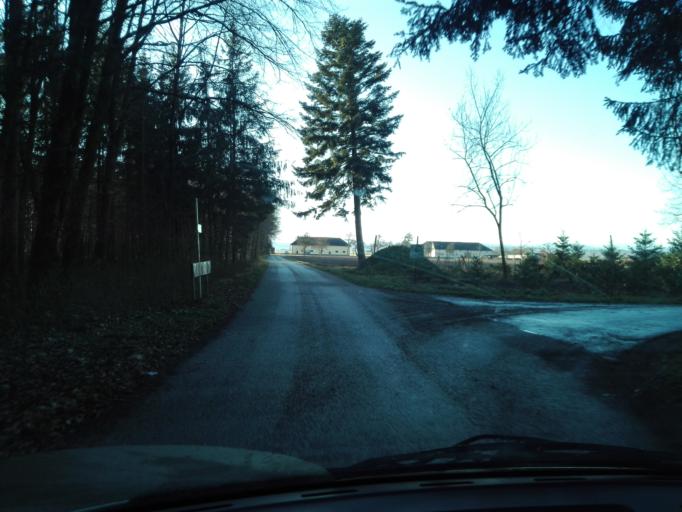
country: AT
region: Upper Austria
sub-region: Politischer Bezirk Perg
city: Perg
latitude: 48.2054
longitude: 14.6771
